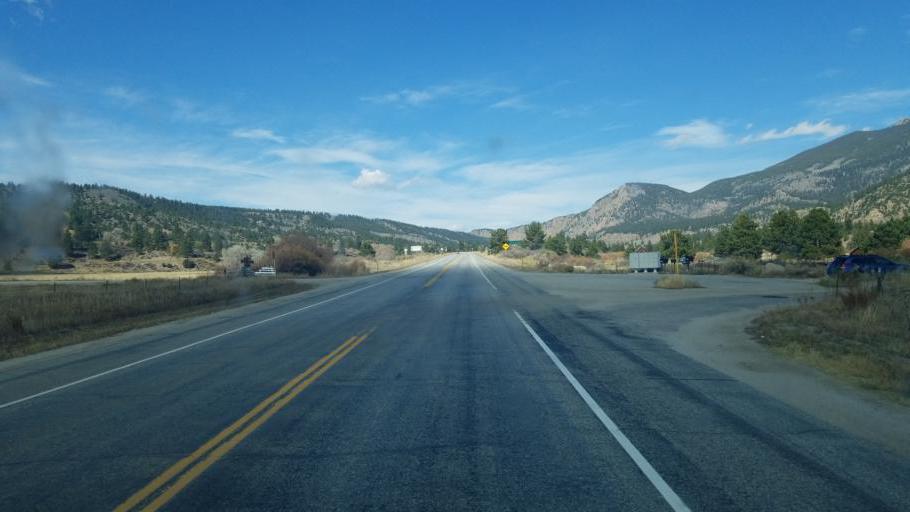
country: US
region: Colorado
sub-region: Chaffee County
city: Buena Vista
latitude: 38.9590
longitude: -106.2018
